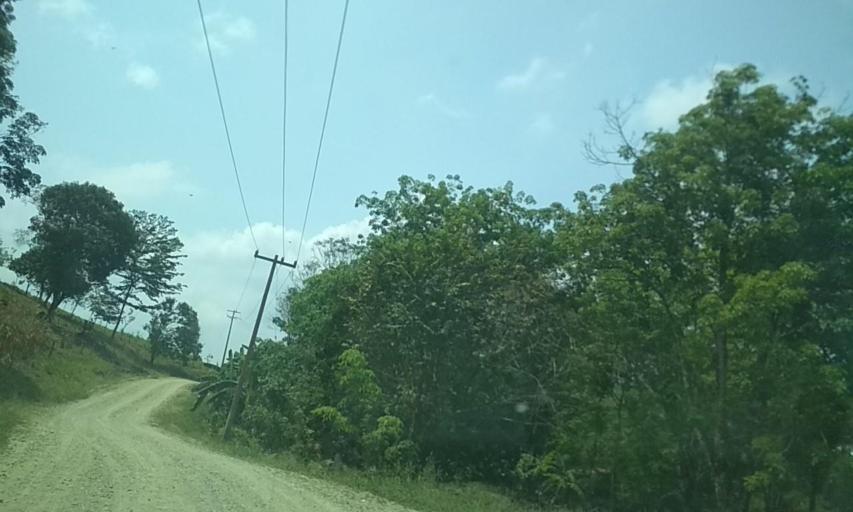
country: MX
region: Tabasco
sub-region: Huimanguillo
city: Francisco Rueda
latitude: 17.6333
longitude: -93.8212
